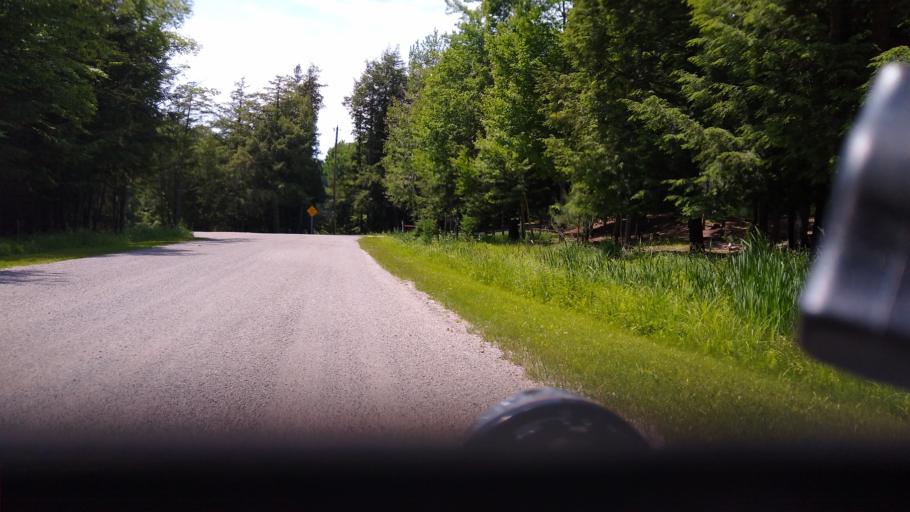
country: US
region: Michigan
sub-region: Delta County
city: Escanaba
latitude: 45.7101
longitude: -87.1587
